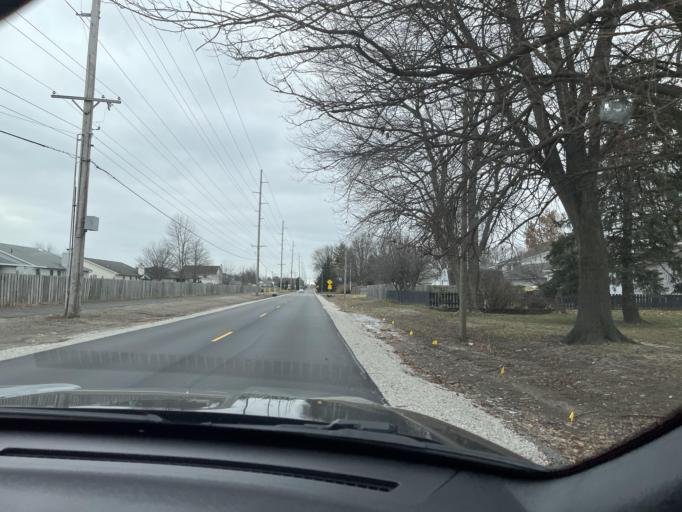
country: US
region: Illinois
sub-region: Sangamon County
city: Rochester
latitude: 39.7649
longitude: -89.5788
